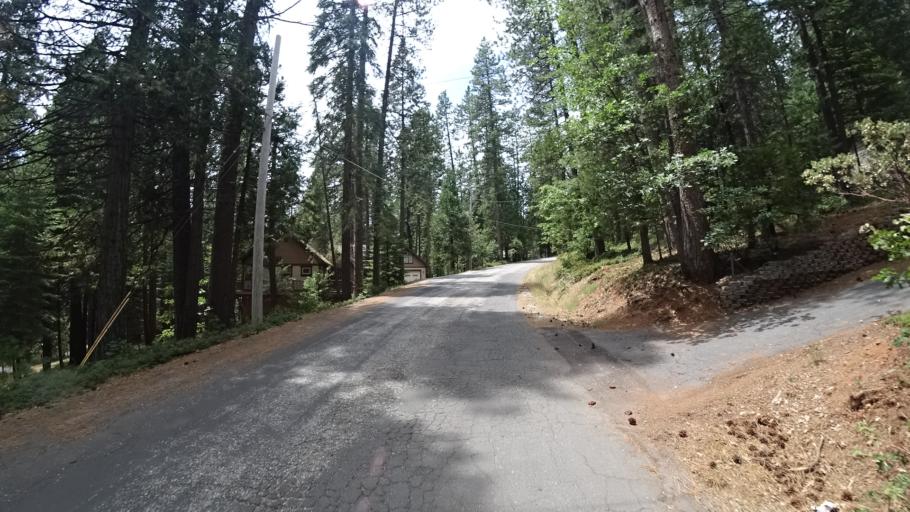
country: US
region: California
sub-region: Calaveras County
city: Arnold
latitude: 38.2343
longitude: -120.3463
